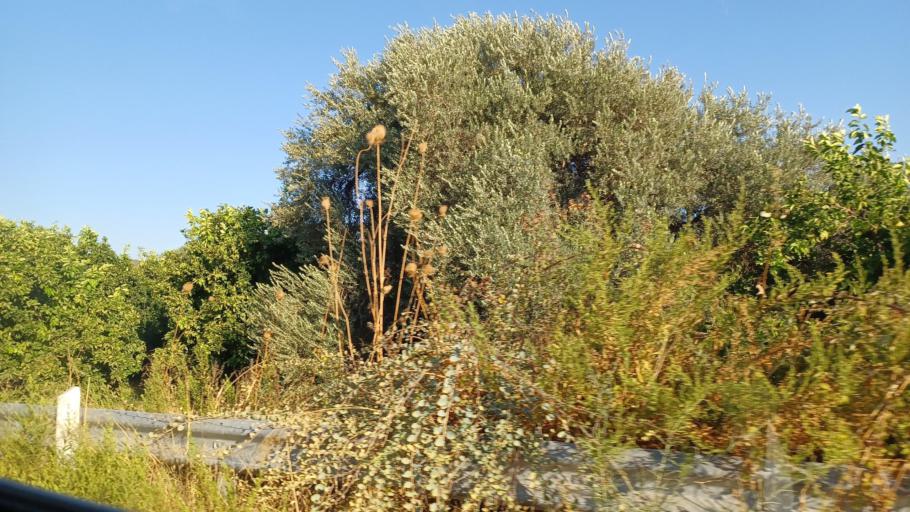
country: CY
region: Pafos
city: Polis
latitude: 35.0019
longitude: 32.4352
